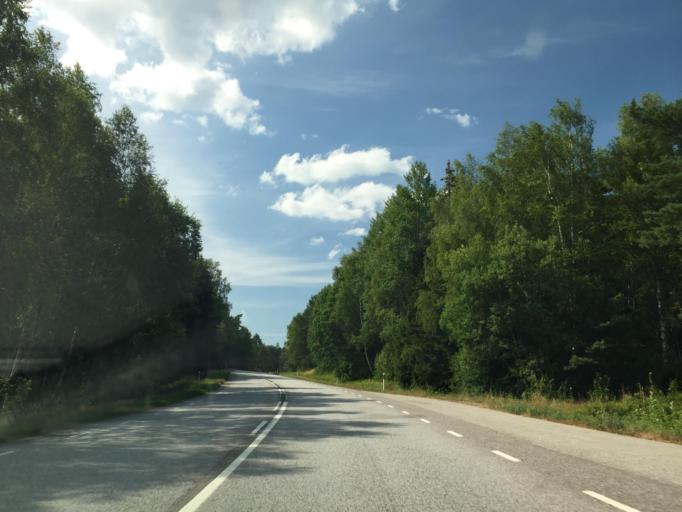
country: SE
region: Vaestra Goetaland
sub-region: Tanums Kommun
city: Grebbestad
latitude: 58.8222
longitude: 11.2565
